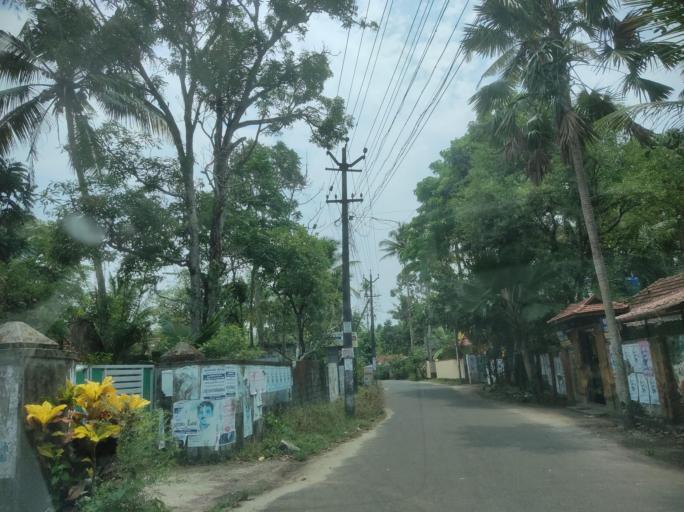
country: IN
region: Kerala
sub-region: Alappuzha
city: Kutiatodu
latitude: 9.7516
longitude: 76.3257
